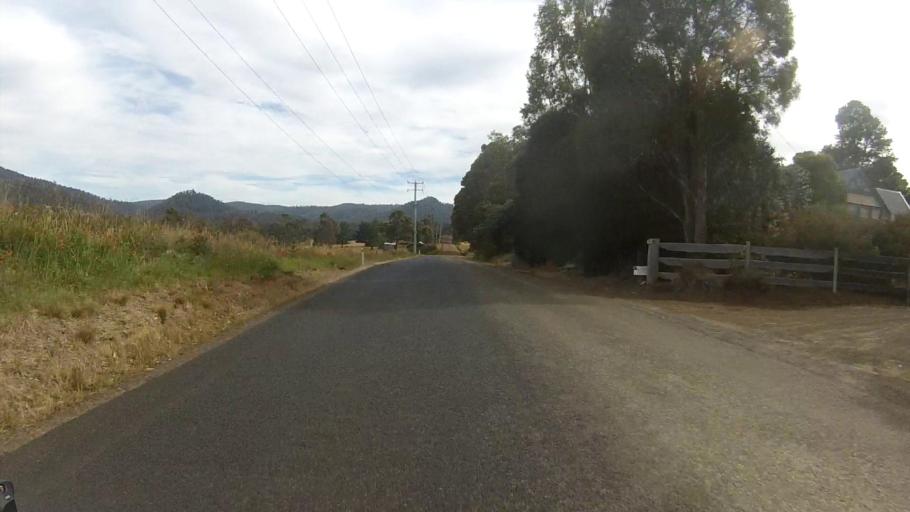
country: AU
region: Tasmania
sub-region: Sorell
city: Sorell
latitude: -42.7873
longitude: 147.8072
